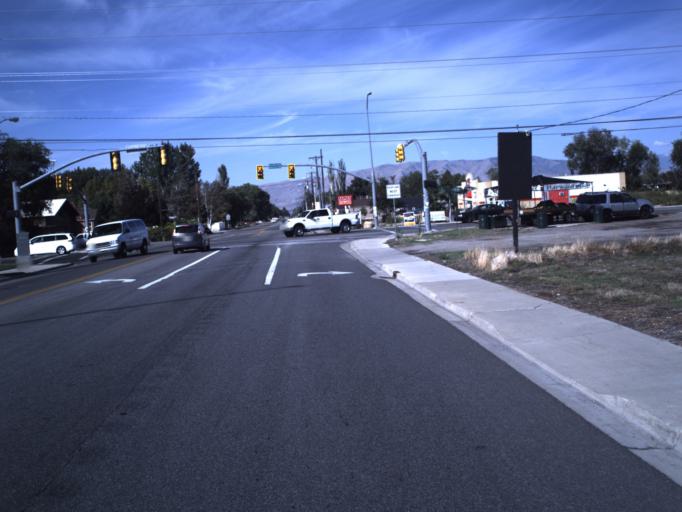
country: US
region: Utah
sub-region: Utah County
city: Provo
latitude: 40.2339
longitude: -111.6940
